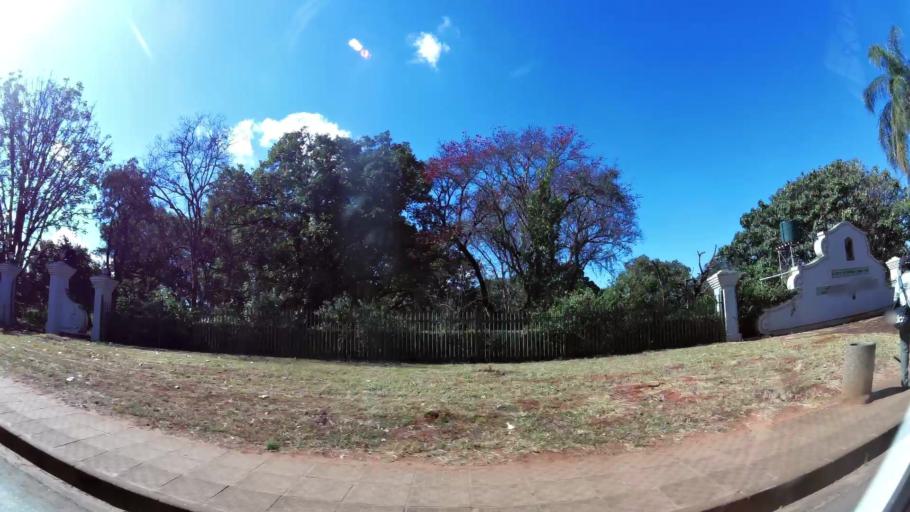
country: ZA
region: Limpopo
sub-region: Mopani District Municipality
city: Tzaneen
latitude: -23.8205
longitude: 30.1587
